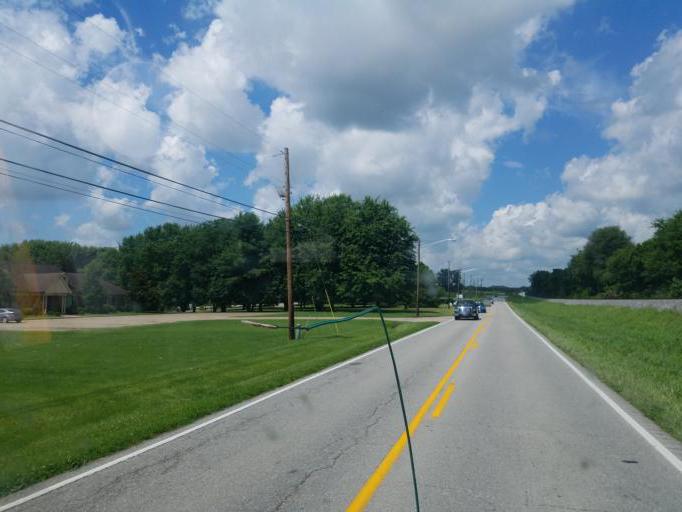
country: US
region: Kentucky
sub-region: Grayson County
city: Leitchfield
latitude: 37.4896
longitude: -86.2556
